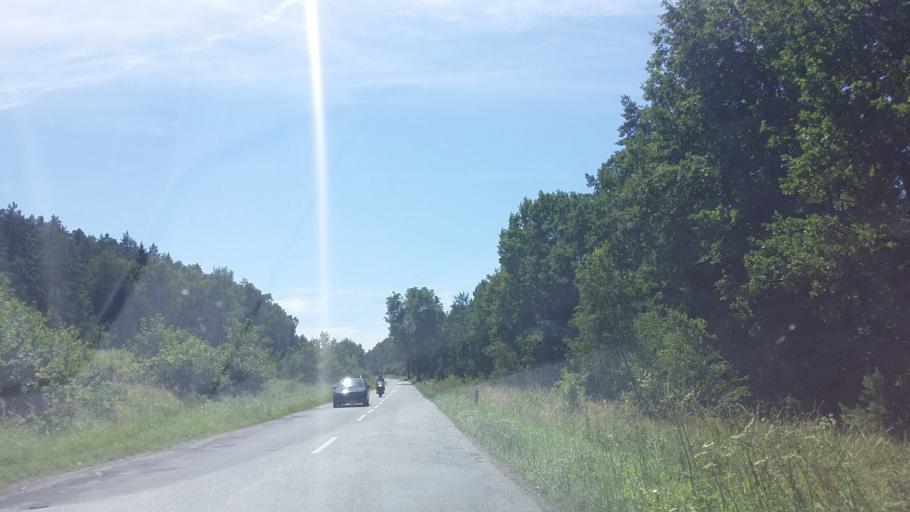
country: PL
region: West Pomeranian Voivodeship
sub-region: Powiat lobeski
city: Lobez
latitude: 53.6645
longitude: 15.6541
